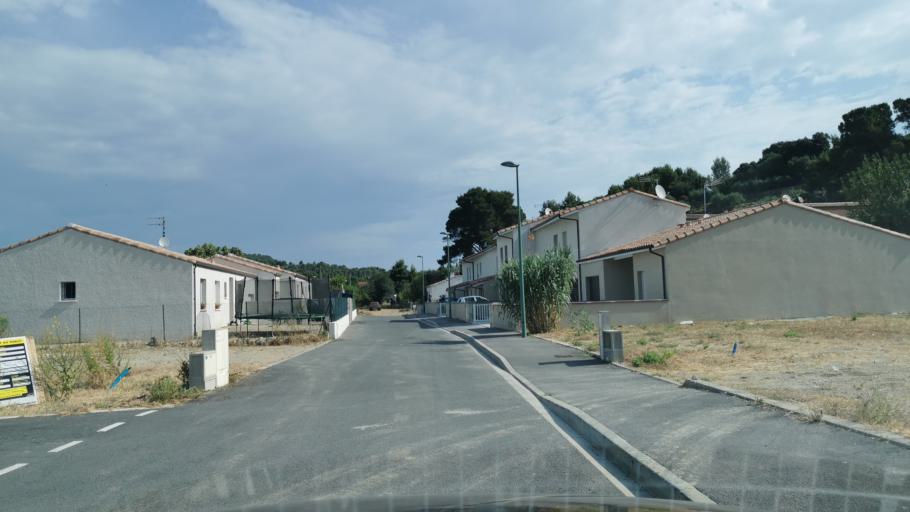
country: FR
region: Languedoc-Roussillon
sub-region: Departement de l'Aude
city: Bize-Minervois
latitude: 43.3135
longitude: 2.8723
